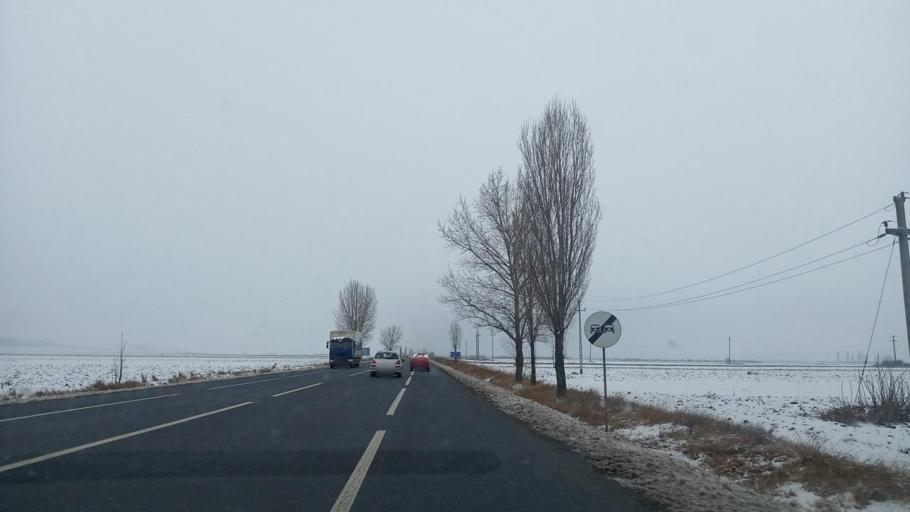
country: RO
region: Vrancea
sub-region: Municipiul  Adjud
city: Adjudu Vechi
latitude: 46.1436
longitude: 27.1481
